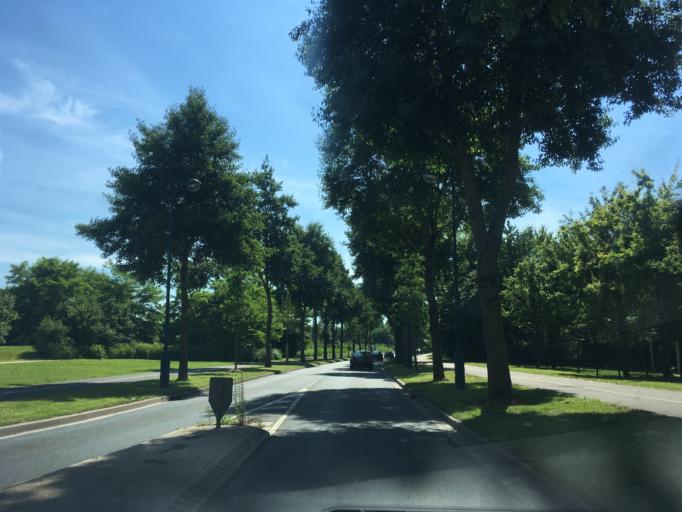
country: FR
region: Ile-de-France
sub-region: Departement de Seine-et-Marne
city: Bailly-Romainvilliers
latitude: 48.8511
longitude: 2.8245
